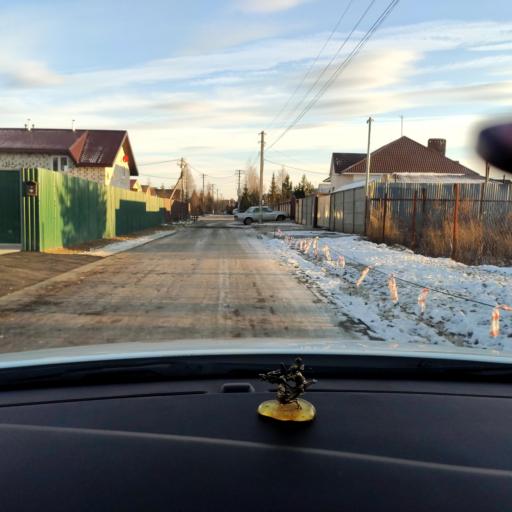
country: RU
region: Tatarstan
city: Stolbishchi
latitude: 55.6079
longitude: 49.1372
